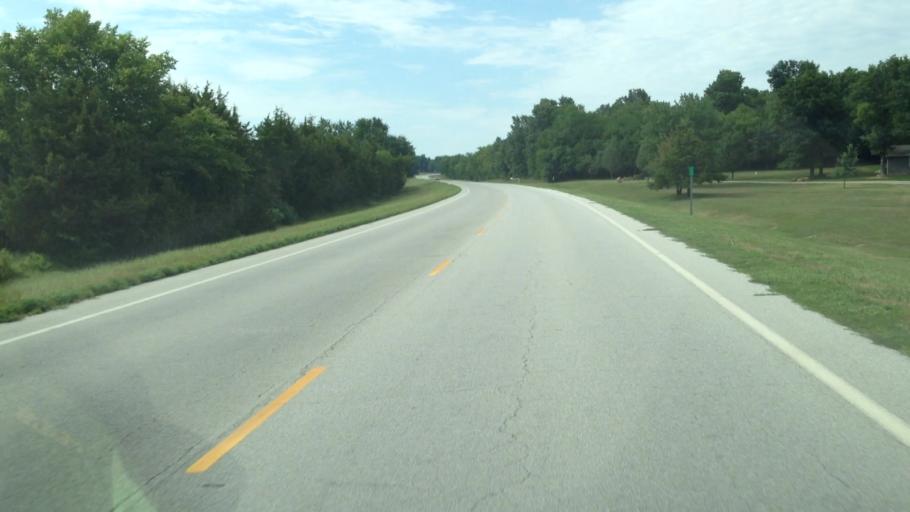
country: US
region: Kansas
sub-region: Labette County
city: Oswego
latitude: 37.1478
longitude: -95.1042
